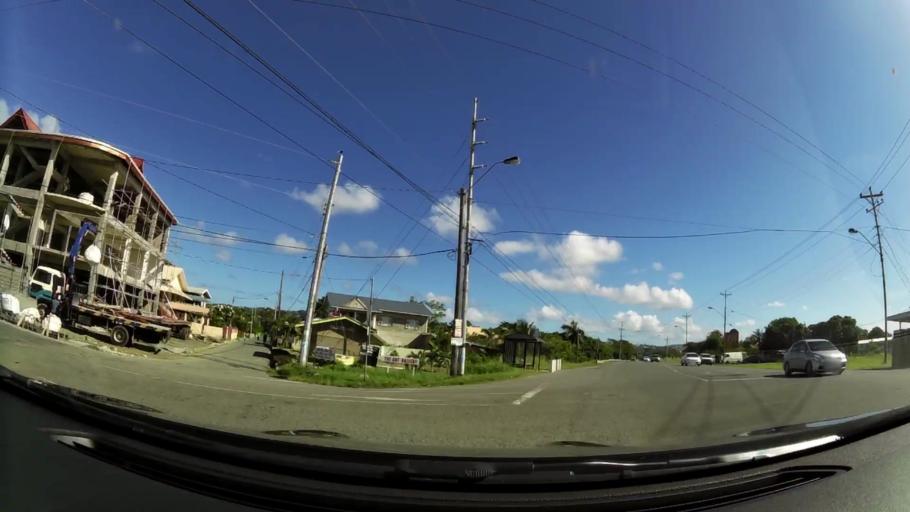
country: TT
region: Tobago
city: Scarborough
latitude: 11.1574
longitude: -60.7828
